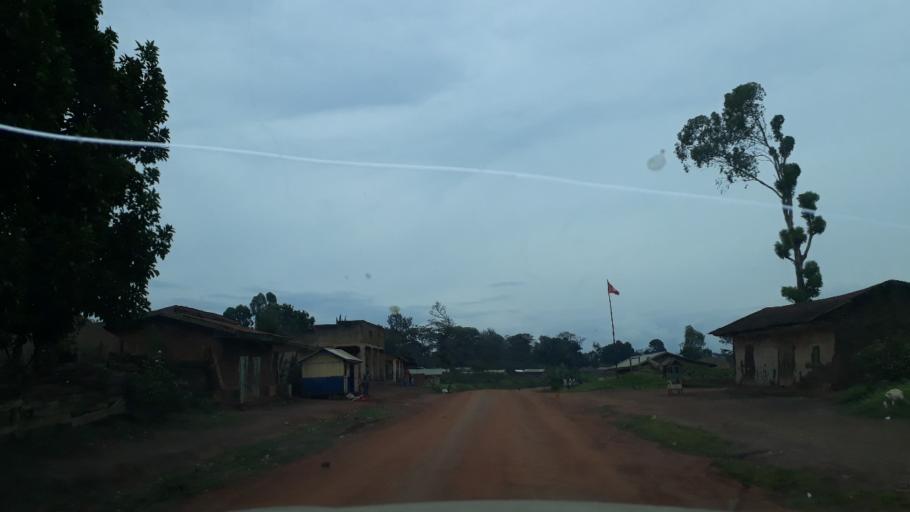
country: UG
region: Northern Region
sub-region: Zombo District
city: Paidha
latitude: 2.1723
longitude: 30.7053
